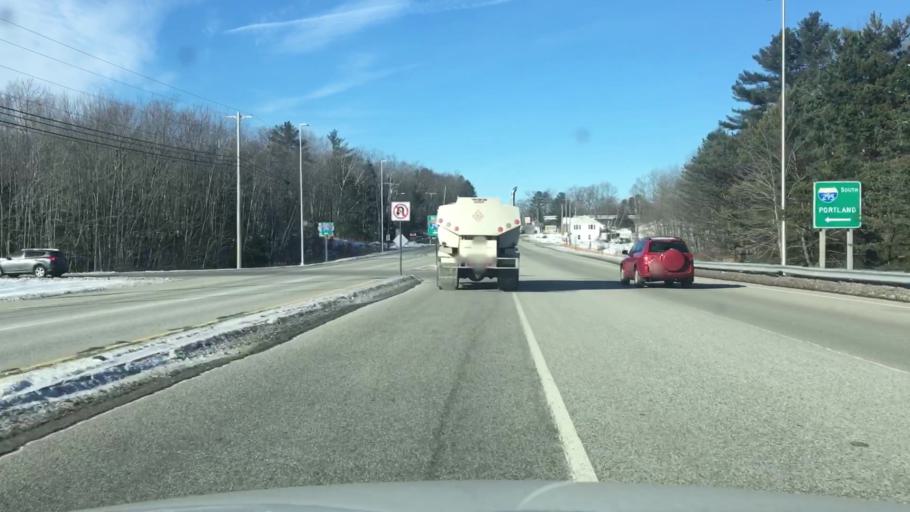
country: US
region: Maine
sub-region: Sagadahoc County
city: Topsham
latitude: 43.9431
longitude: -69.9807
